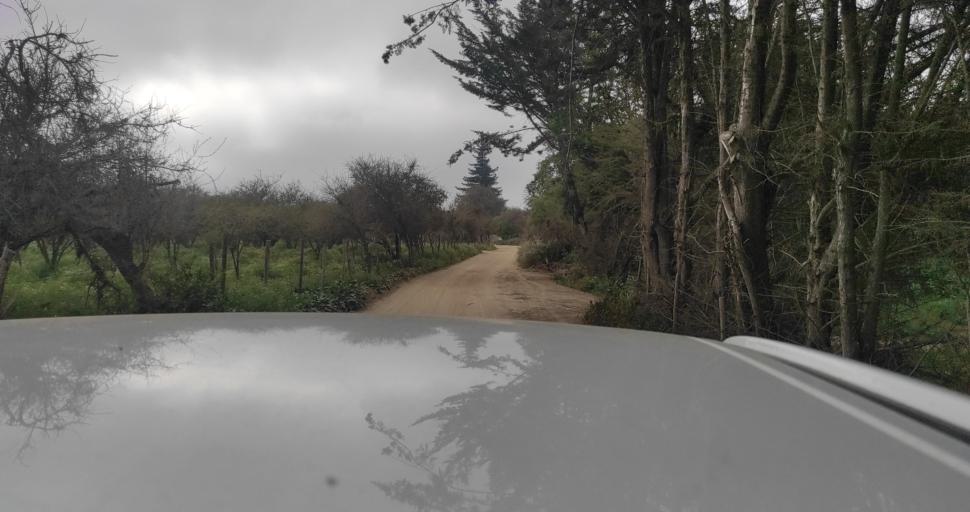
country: CL
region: Valparaiso
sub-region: Provincia de Marga Marga
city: Villa Alemana
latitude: -33.3598
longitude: -71.3075
